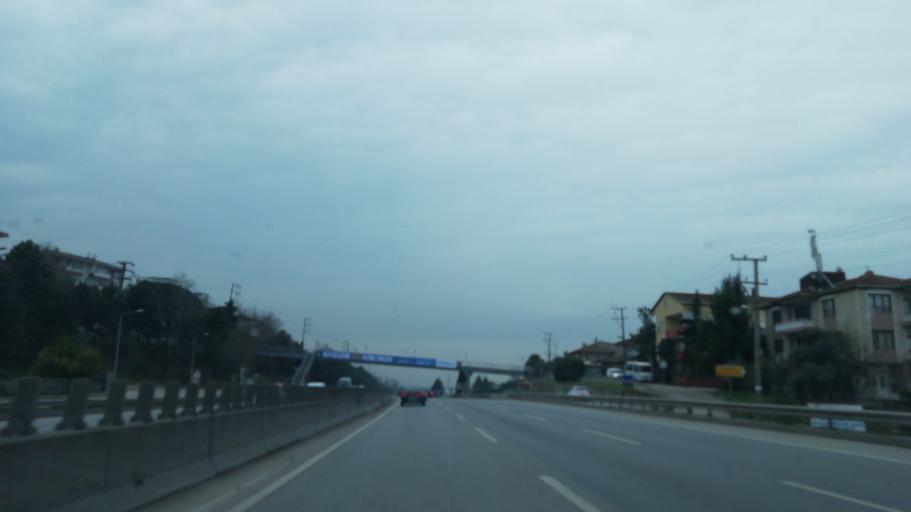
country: TR
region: Kocaeli
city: Derince
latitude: 40.7617
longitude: 29.8586
